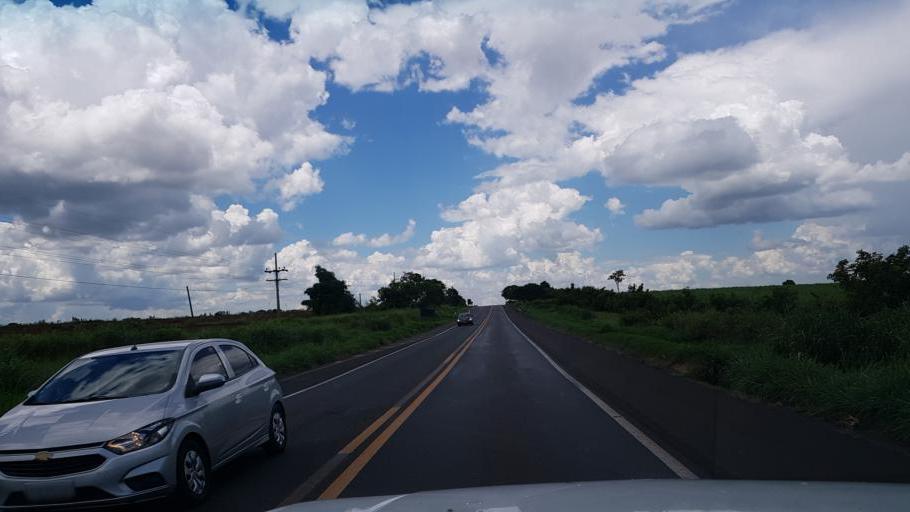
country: BR
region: Sao Paulo
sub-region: Paraguacu Paulista
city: Paraguacu Paulista
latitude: -22.3783
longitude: -50.6202
